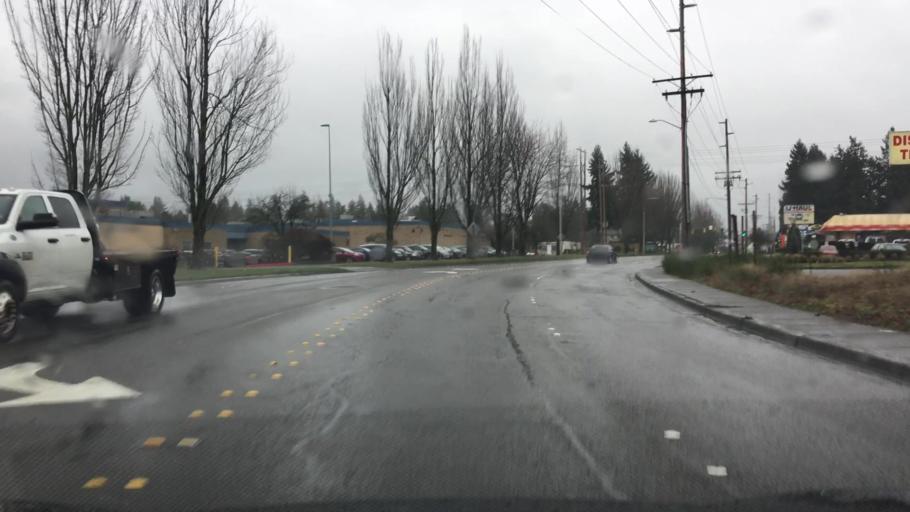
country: US
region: Washington
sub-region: King County
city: Renton
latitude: 47.4884
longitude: -122.1783
